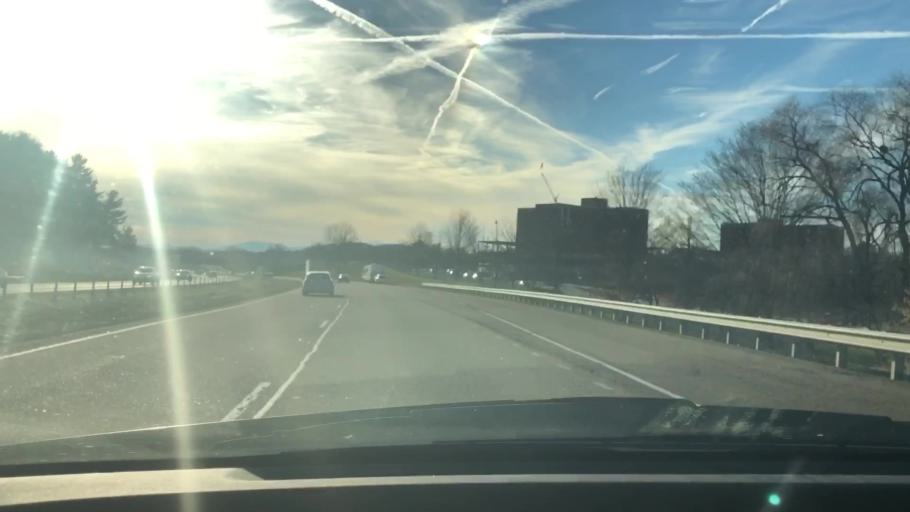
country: US
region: Virginia
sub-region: City of Harrisonburg
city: Harrisonburg
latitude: 38.4347
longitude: -78.8690
